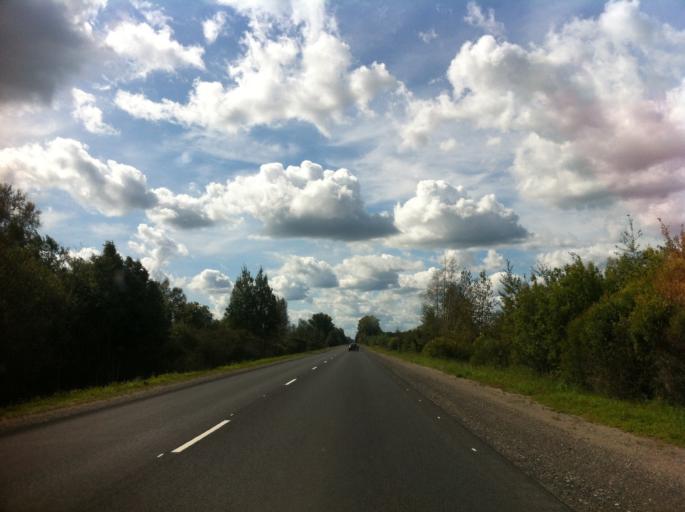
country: RU
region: Pskov
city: Izborsk
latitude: 57.7369
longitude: 27.9969
